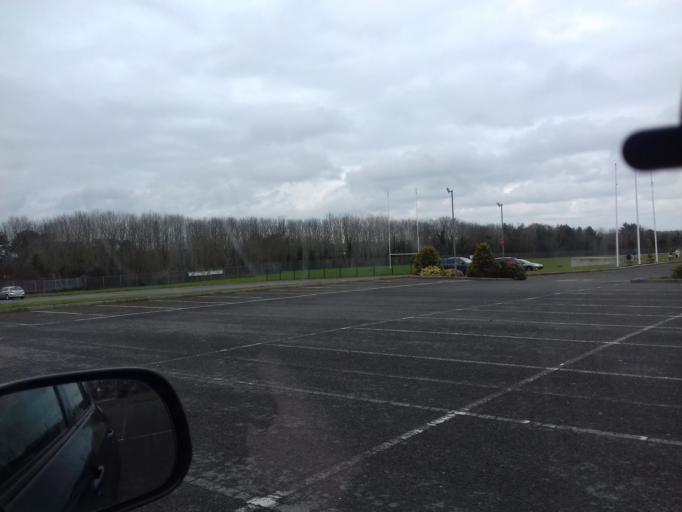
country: IE
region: Leinster
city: Portmarnock
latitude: 53.4376
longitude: -6.1417
